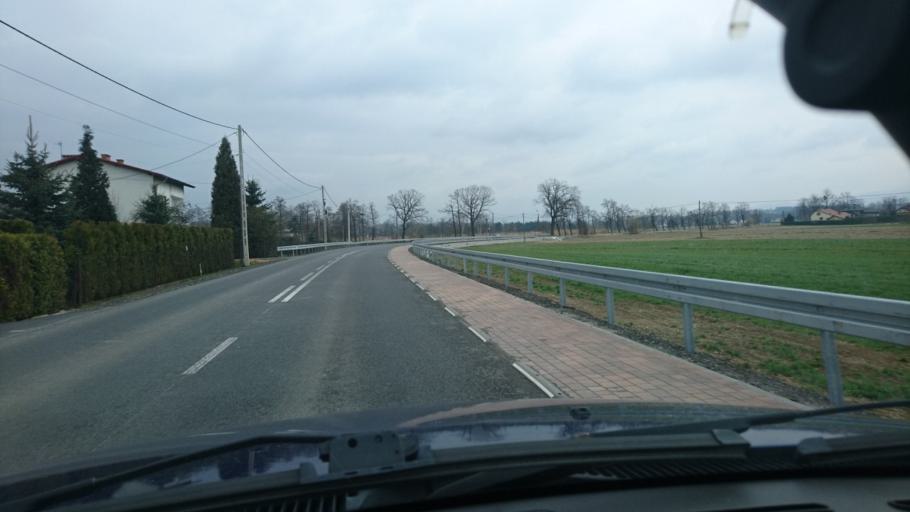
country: PL
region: Silesian Voivodeship
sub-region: Powiat bielski
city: Bronow
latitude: 49.8808
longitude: 18.9386
